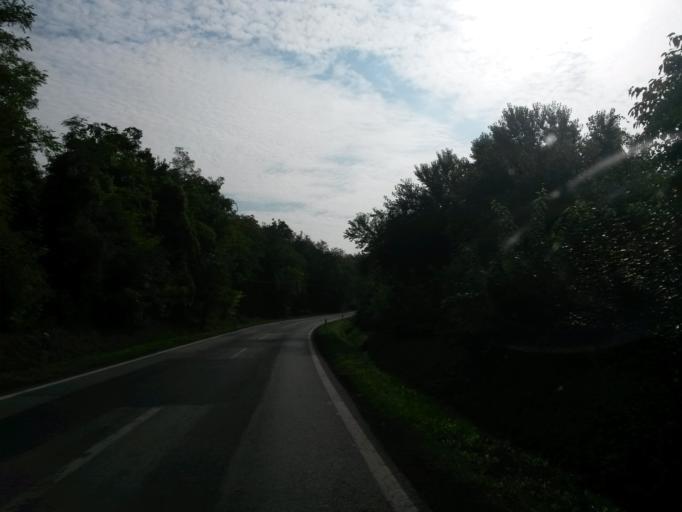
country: HR
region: Vukovarsko-Srijemska
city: Ilok
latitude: 45.2243
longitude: 19.3420
